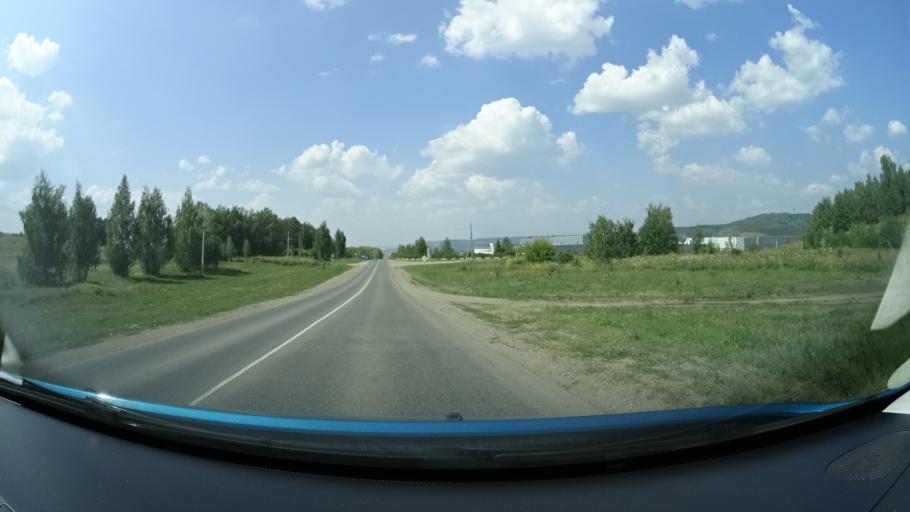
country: RU
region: Bashkortostan
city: Oktyabr'skiy
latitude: 54.4789
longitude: 53.5635
